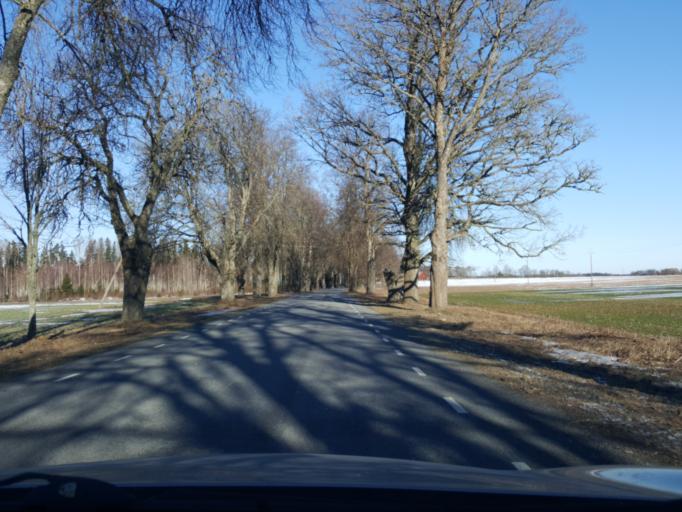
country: EE
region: Viljandimaa
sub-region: Vohma linn
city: Vohma
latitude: 58.5336
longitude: 25.5831
